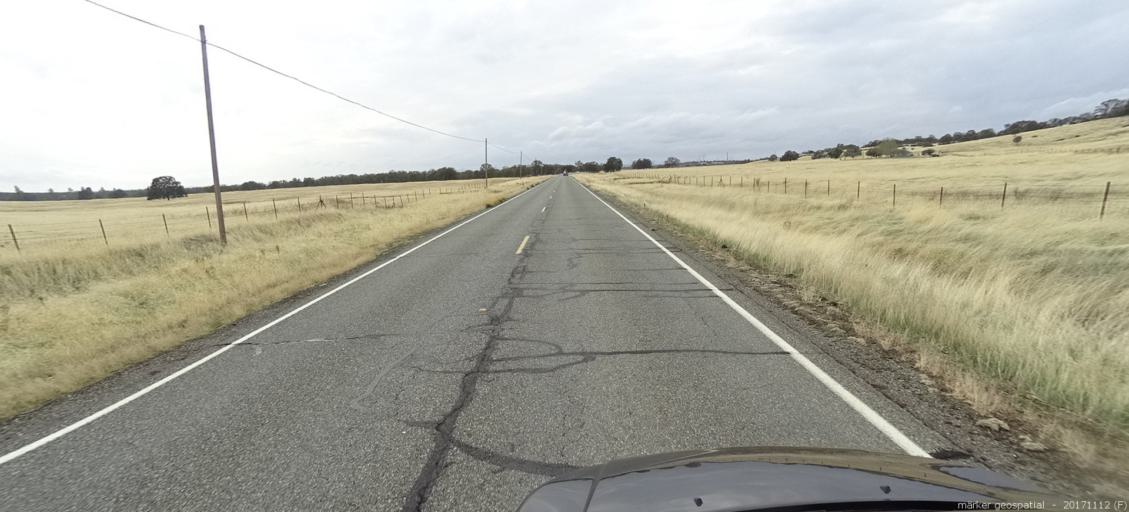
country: US
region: California
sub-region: Shasta County
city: Palo Cedro
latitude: 40.4797
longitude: -122.1708
